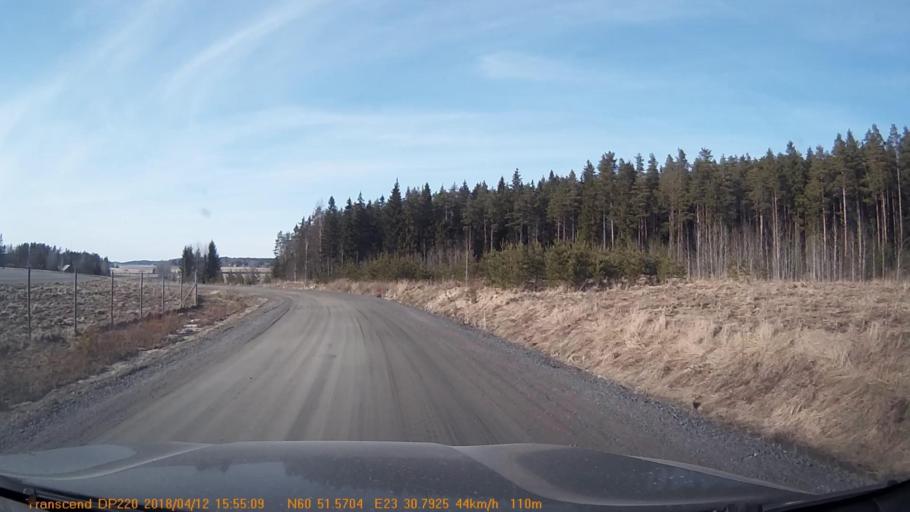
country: FI
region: Haeme
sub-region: Forssa
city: Jokioinen
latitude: 60.8595
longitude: 23.5132
